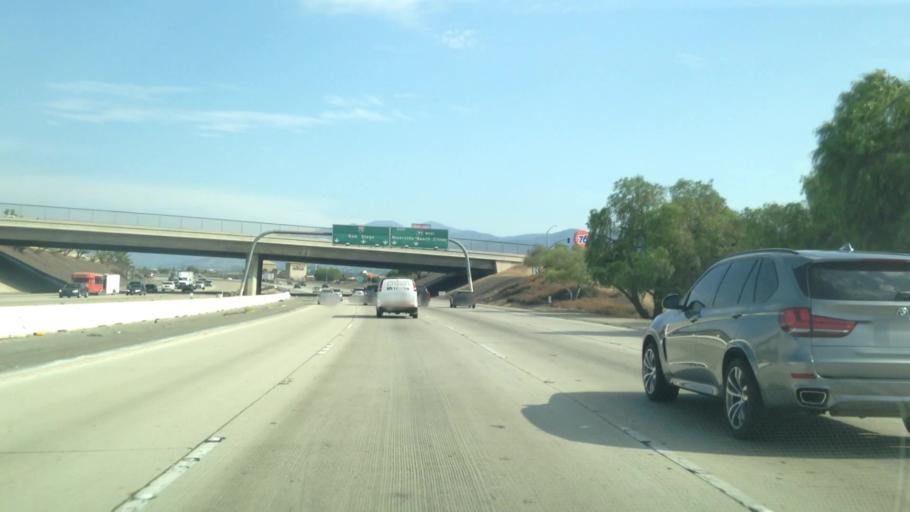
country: US
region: California
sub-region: Riverside County
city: Corona
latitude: 33.9002
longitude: -117.5603
